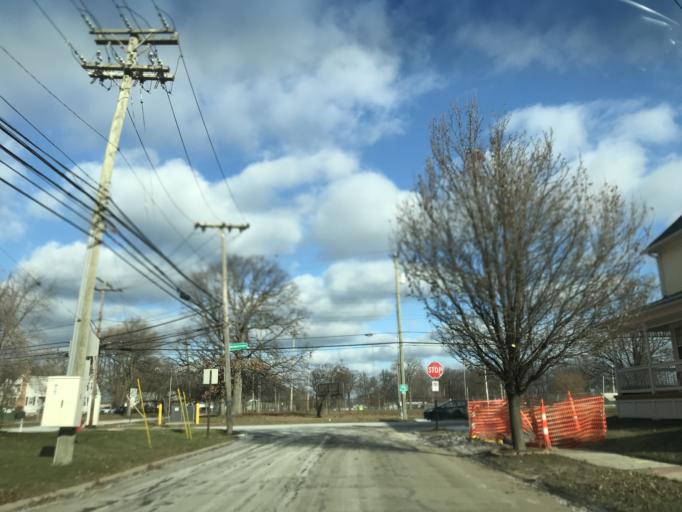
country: US
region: Michigan
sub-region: Oakland County
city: Hazel Park
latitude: 42.4680
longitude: -83.1133
